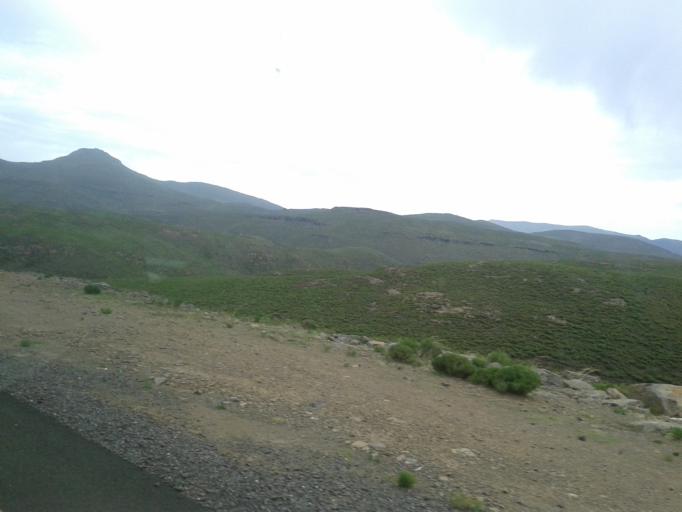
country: LS
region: Maseru
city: Nako
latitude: -29.7536
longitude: 27.9773
